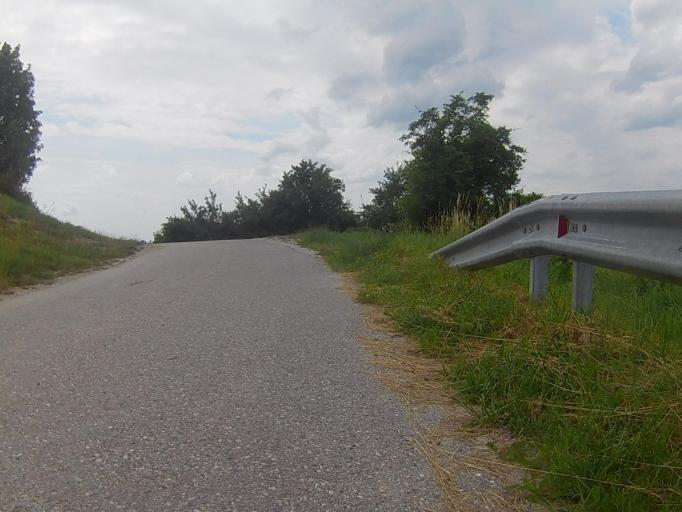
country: SI
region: Sentilj
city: Sentilj v Slov. Goricah
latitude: 46.6714
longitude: 15.6399
